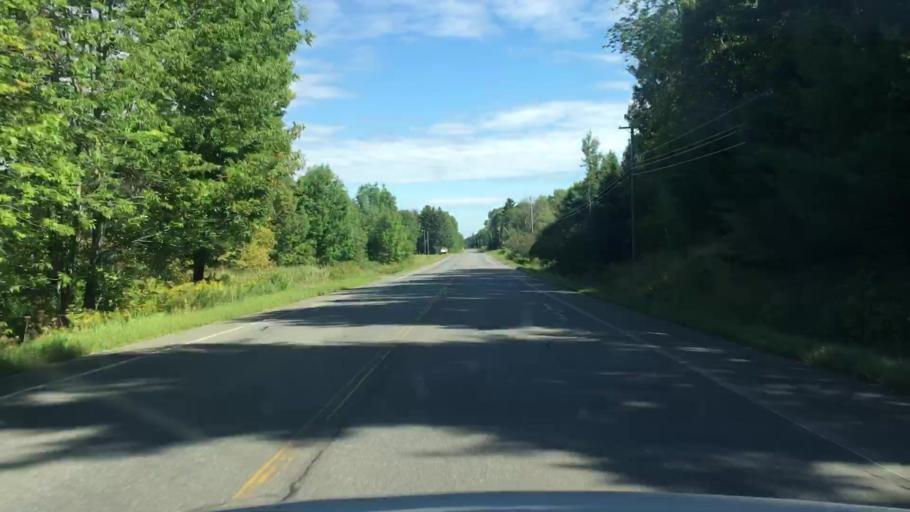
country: US
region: Maine
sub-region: Penobscot County
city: Dexter
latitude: 45.0609
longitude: -69.2496
